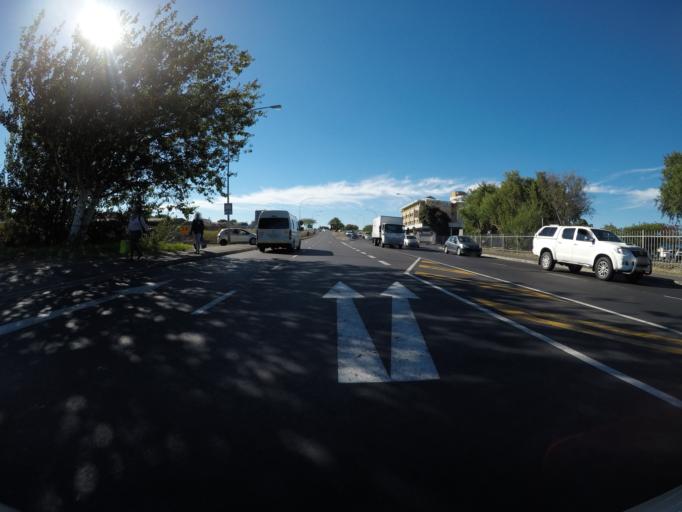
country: ZA
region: Western Cape
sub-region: City of Cape Town
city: Kraaifontein
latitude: -33.9202
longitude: 18.6753
